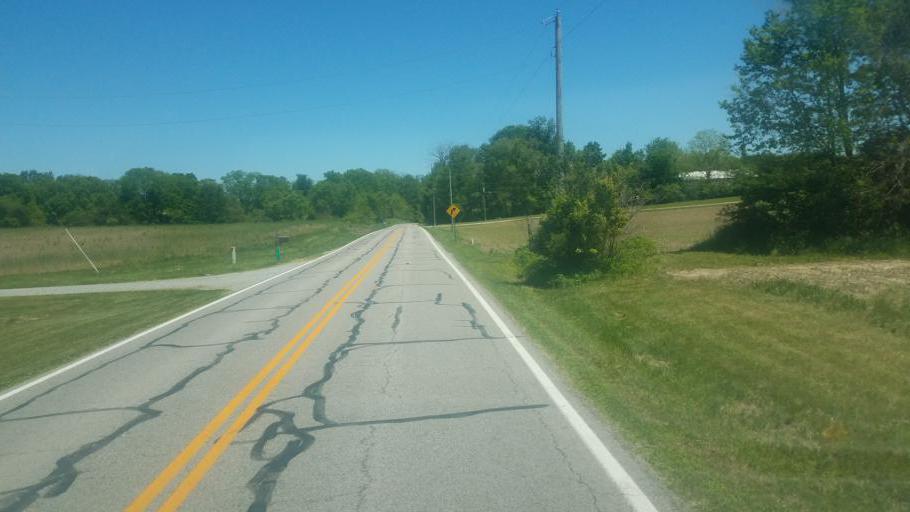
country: US
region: Ohio
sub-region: Miami County
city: Piqua
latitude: 40.2111
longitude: -84.2577
